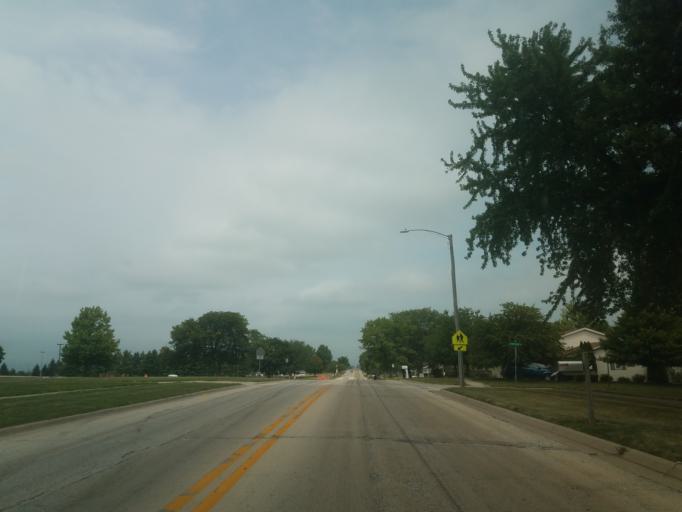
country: US
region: Illinois
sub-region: McLean County
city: Normal
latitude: 40.5119
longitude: -89.0211
